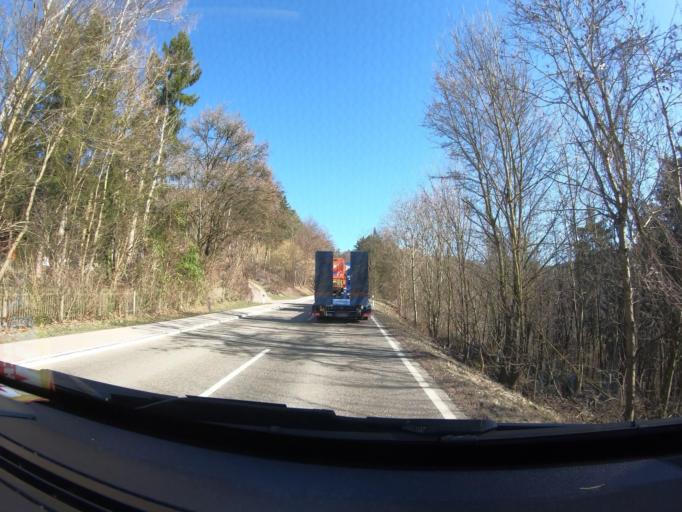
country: DE
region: Baden-Wuerttemberg
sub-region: Regierungsbezirk Stuttgart
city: Gaildorf
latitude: 49.0131
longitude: 9.7825
